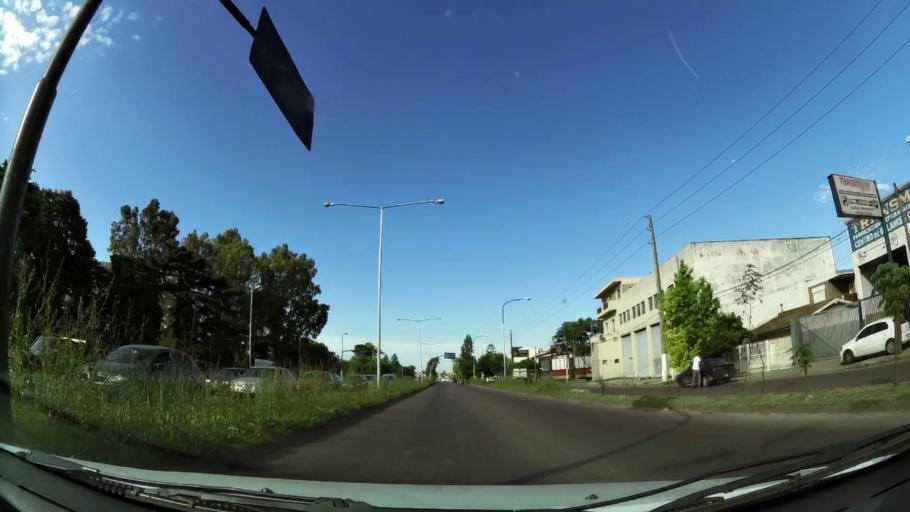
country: AR
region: Buenos Aires
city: Hurlingham
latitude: -34.5842
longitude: -58.6040
